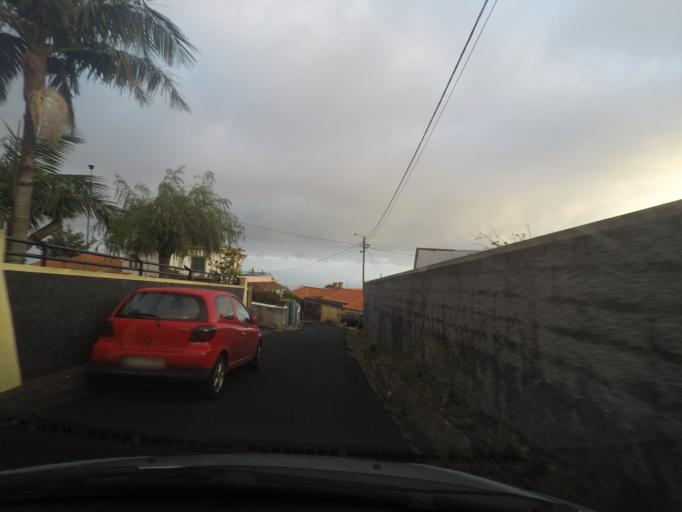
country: PT
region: Madeira
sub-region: Santa Cruz
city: Camacha
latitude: 32.6803
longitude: -16.8517
